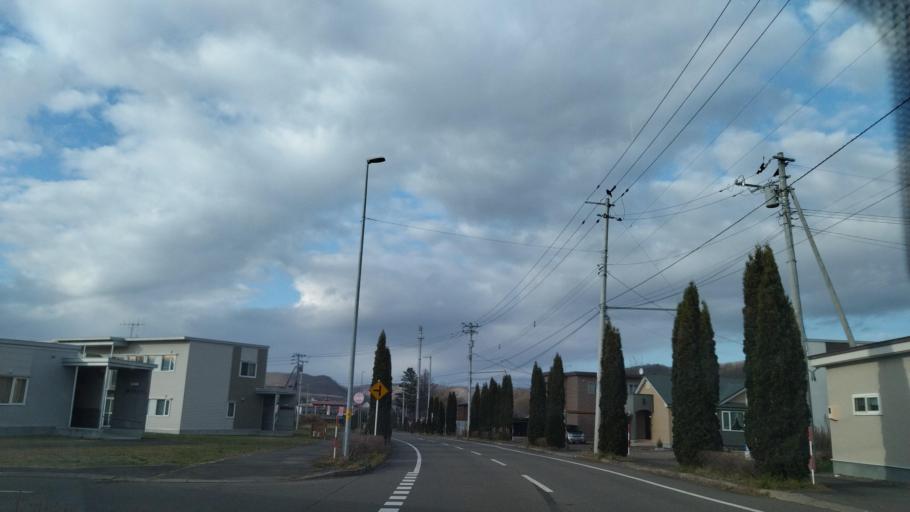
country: JP
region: Hokkaido
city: Otofuke
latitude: 43.2477
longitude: 143.5525
